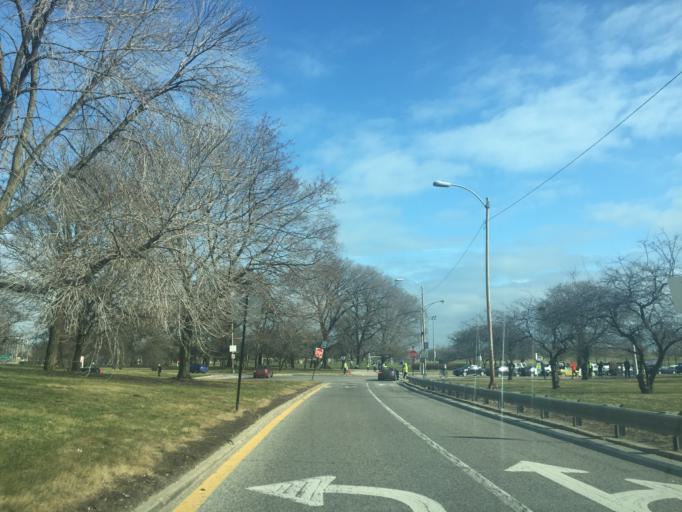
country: US
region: Illinois
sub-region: Cook County
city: Evanston
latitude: 41.9615
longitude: -87.6457
